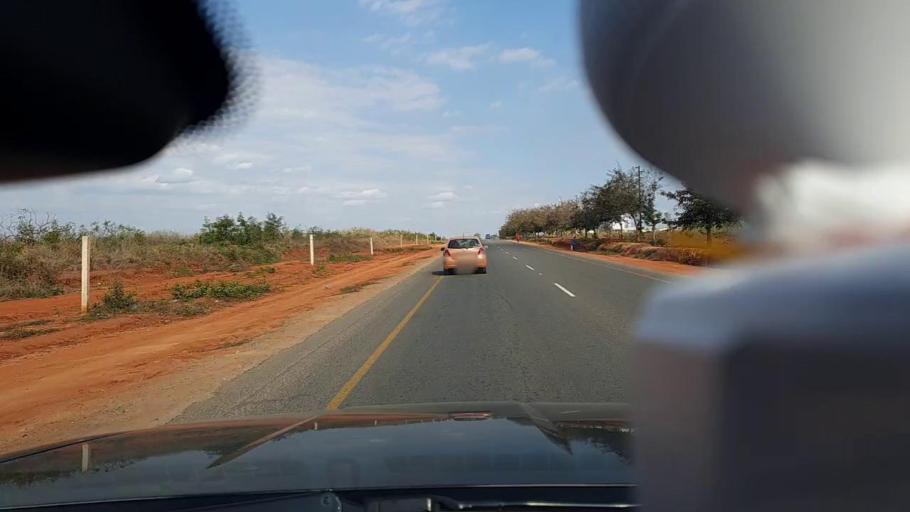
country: MZ
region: Nampula
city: Nampula
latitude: -15.1522
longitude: 39.3019
